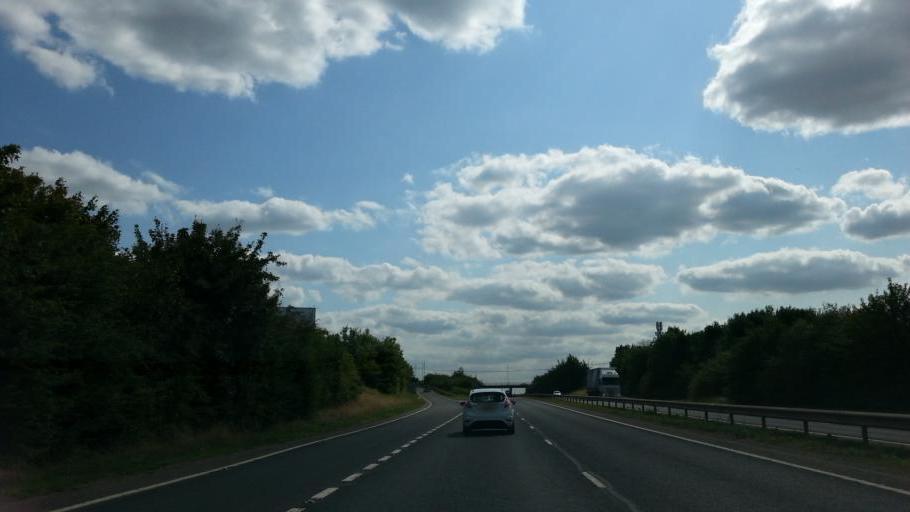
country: GB
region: England
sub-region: Leicestershire
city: Mountsorrel
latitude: 52.7229
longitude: -1.1283
